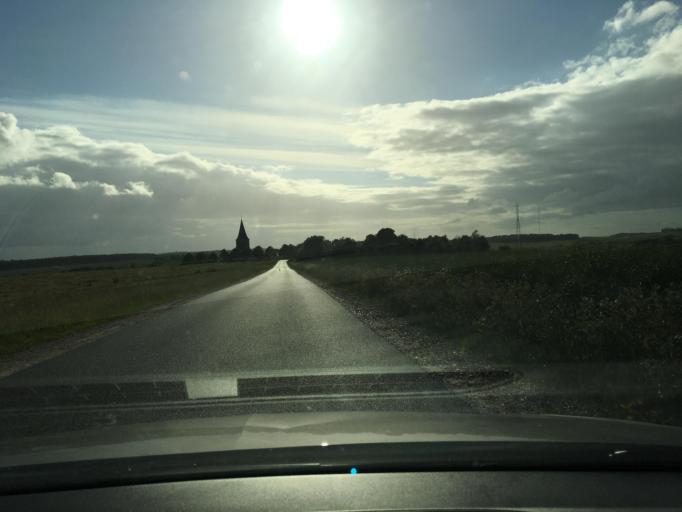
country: DK
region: Central Jutland
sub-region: Favrskov Kommune
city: Hinnerup
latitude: 56.2794
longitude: 10.0494
